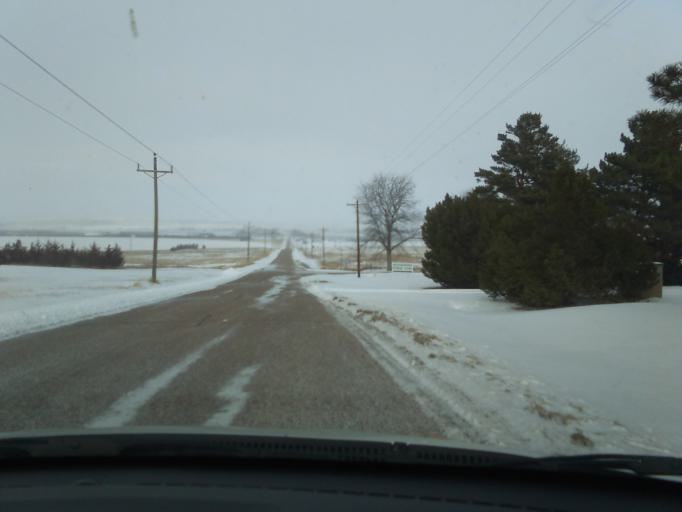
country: US
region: Nebraska
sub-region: Kimball County
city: Kimball
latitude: 41.2254
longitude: -103.6245
